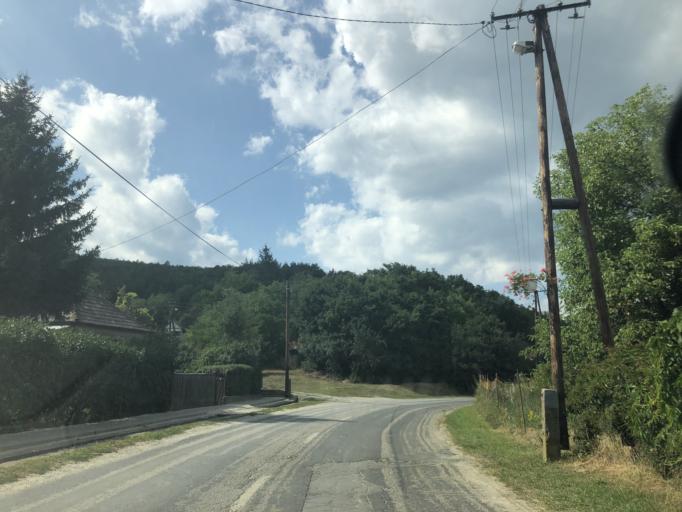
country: HU
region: Borsod-Abauj-Zemplen
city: Szendro
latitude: 48.4416
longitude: 20.7934
